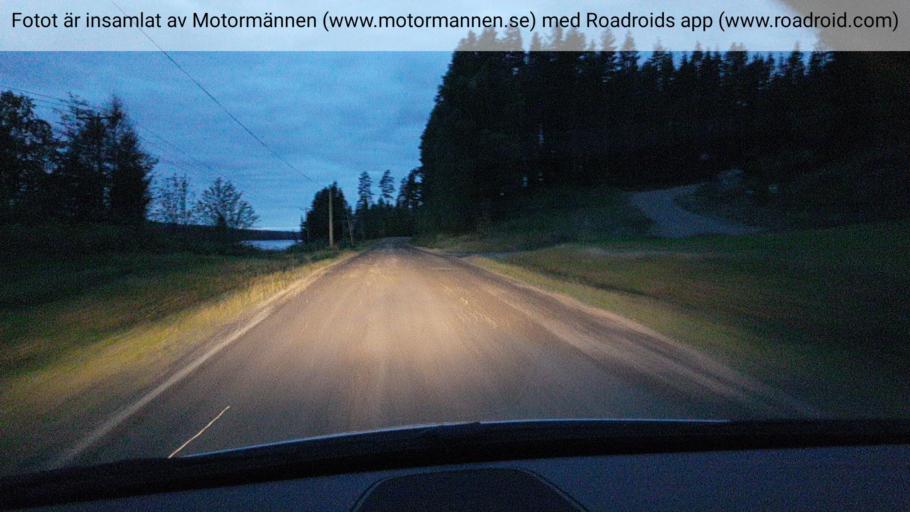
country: SE
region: Jaemtland
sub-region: Braecke Kommun
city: Braecke
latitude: 63.1971
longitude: 15.4688
